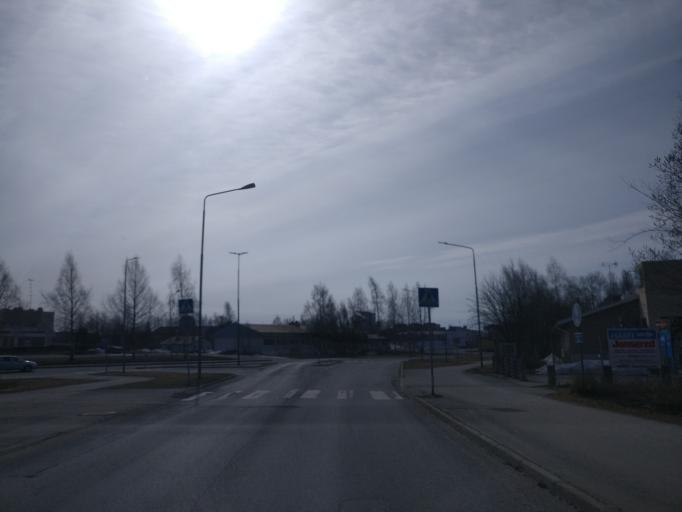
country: FI
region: Lapland
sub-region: Kemi-Tornio
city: Kemi
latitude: 65.7436
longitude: 24.5659
